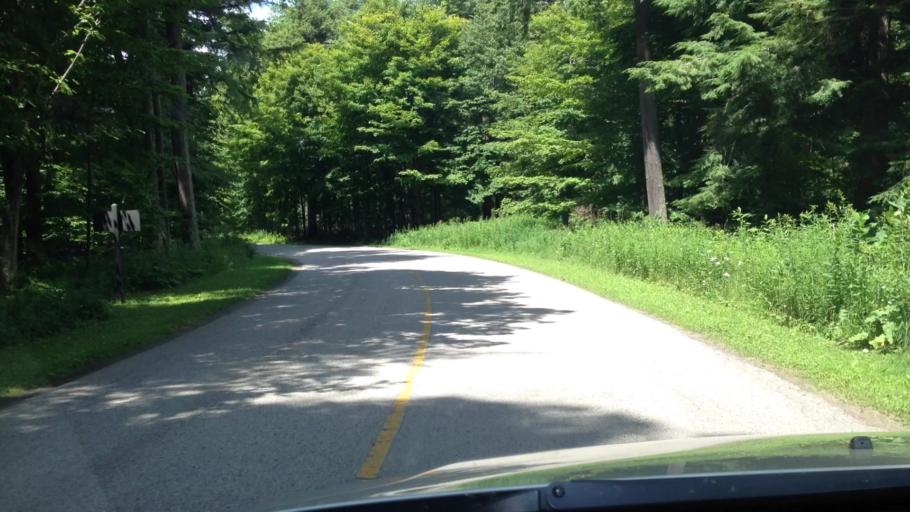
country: US
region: Michigan
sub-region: Menominee County
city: Menominee
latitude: 45.3946
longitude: -87.3656
